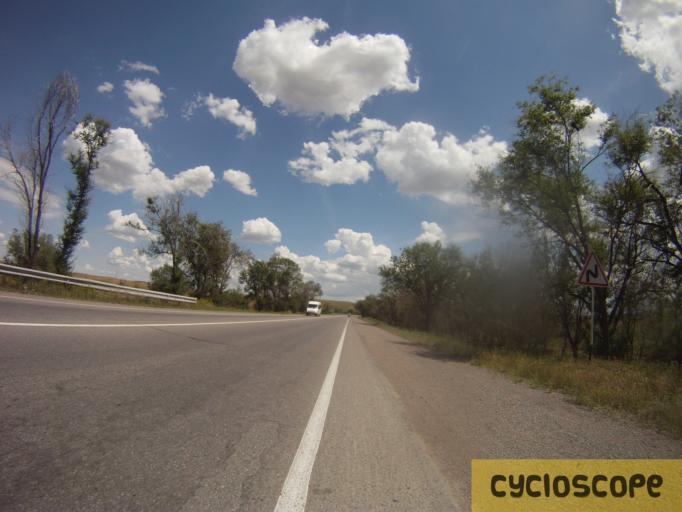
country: KZ
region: Almaty Oblysy
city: Burunday
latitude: 43.3149
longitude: 76.1691
